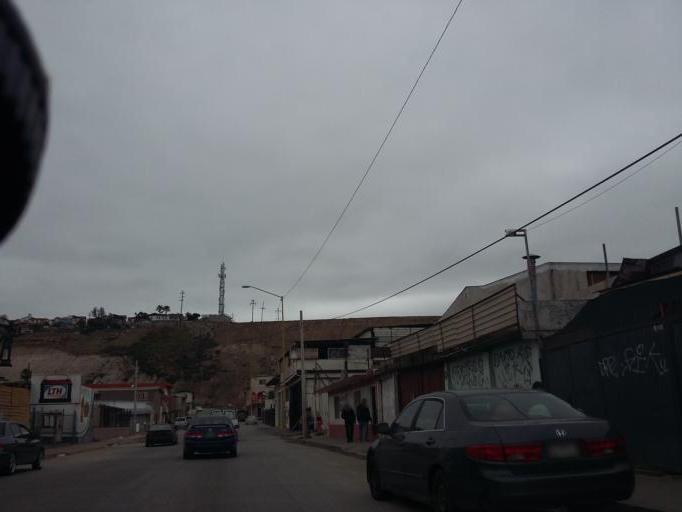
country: MX
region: Baja California
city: Tijuana
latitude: 32.5247
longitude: -116.9257
